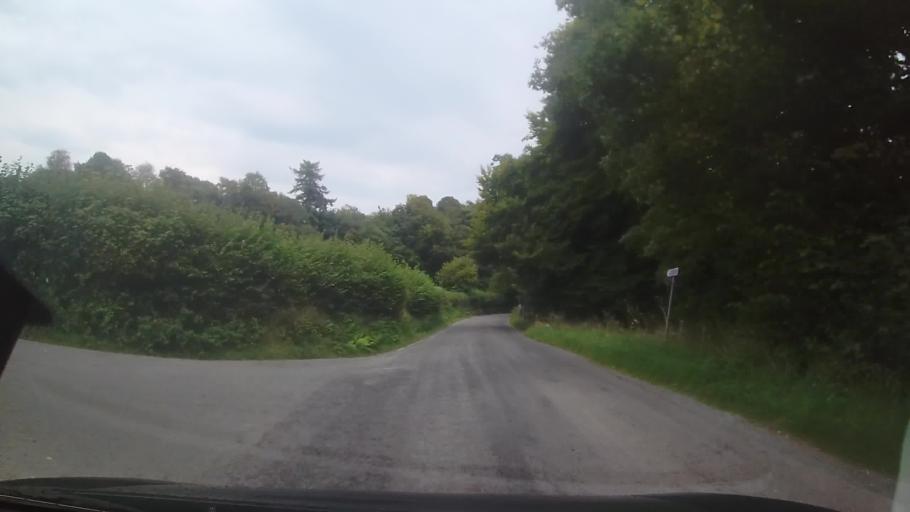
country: GB
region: Wales
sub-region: Sir Powys
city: Rhayader
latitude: 52.3036
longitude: -3.5282
